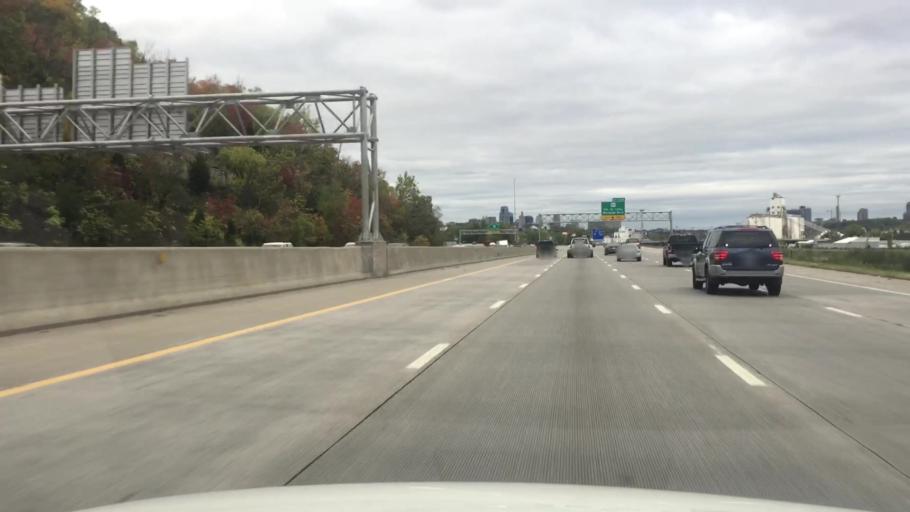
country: US
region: Kansas
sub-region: Johnson County
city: Westwood
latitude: 39.0644
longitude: -94.6236
